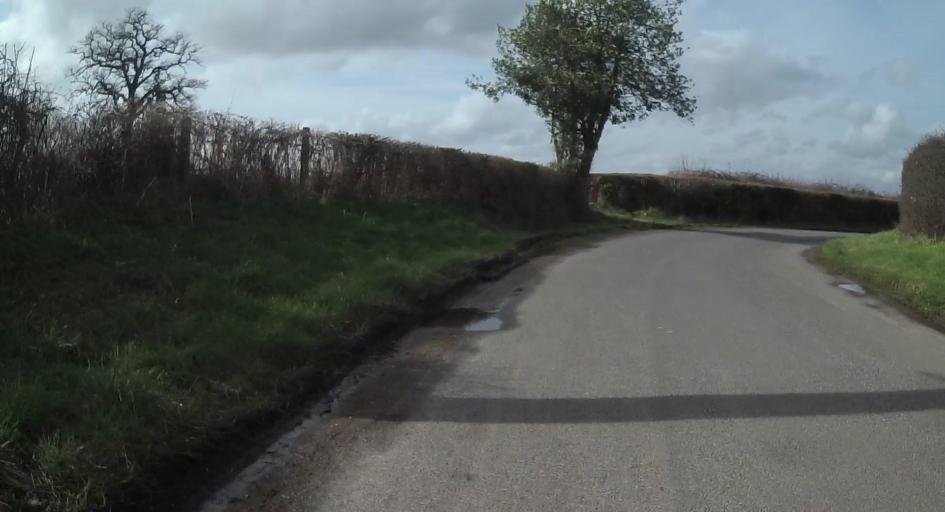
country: GB
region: England
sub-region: Hampshire
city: Kingsclere
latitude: 51.3396
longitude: -1.2428
